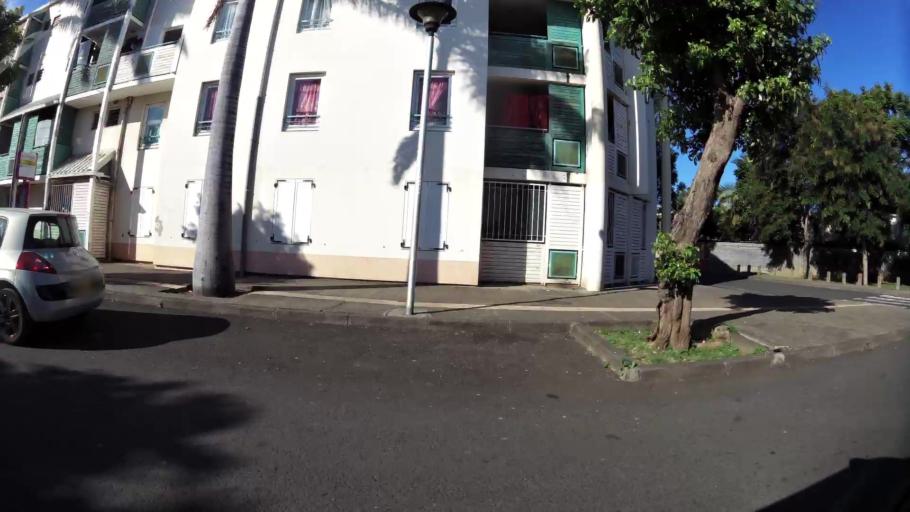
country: RE
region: Reunion
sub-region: Reunion
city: Saint-Louis
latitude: -21.2874
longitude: 55.4175
